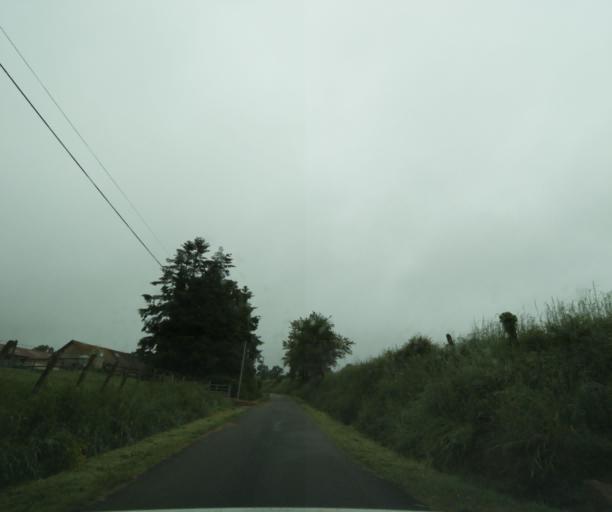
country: FR
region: Bourgogne
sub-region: Departement de Saone-et-Loire
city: Charolles
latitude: 46.3976
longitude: 4.3846
